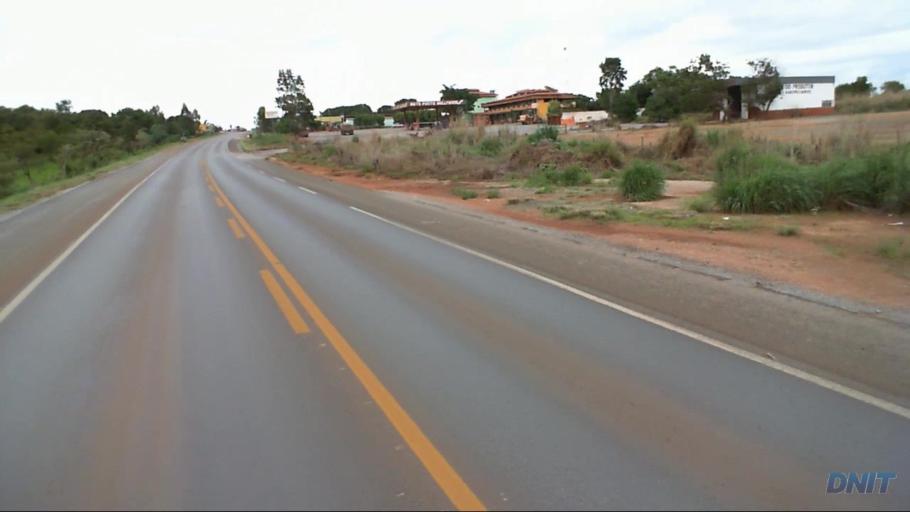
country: BR
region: Goias
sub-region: Barro Alto
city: Barro Alto
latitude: -15.2090
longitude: -48.6957
